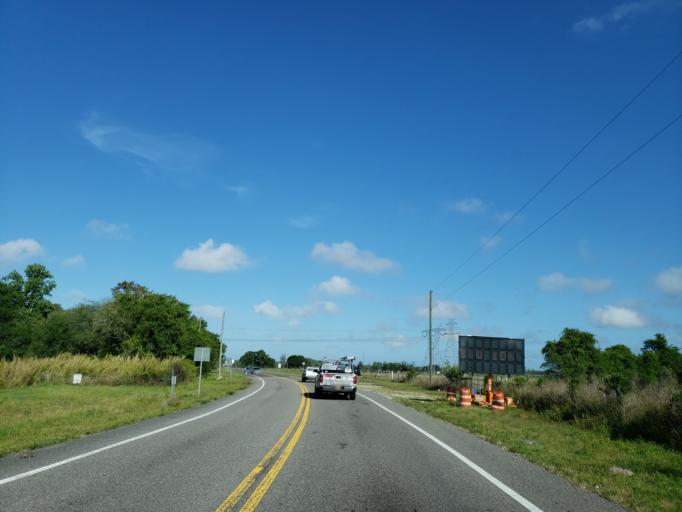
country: US
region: Florida
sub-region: Hillsborough County
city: Keystone
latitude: 28.1447
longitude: -82.6497
